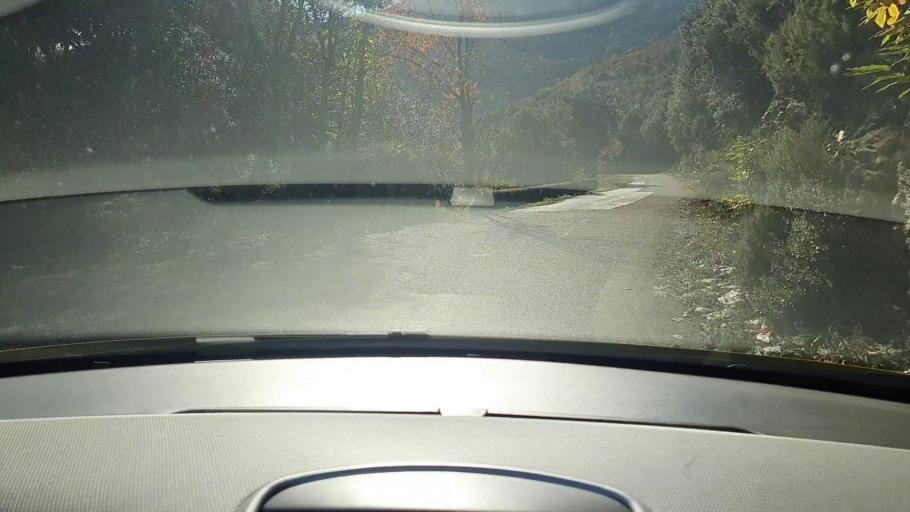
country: FR
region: Languedoc-Roussillon
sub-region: Departement du Gard
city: Valleraugue
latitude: 44.1725
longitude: 3.6545
